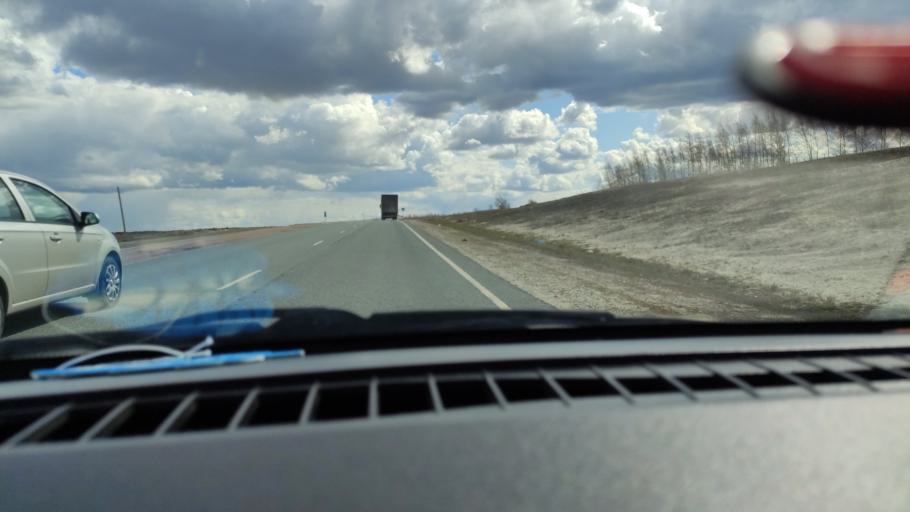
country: RU
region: Samara
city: Syzran'
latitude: 52.9546
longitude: 48.3075
